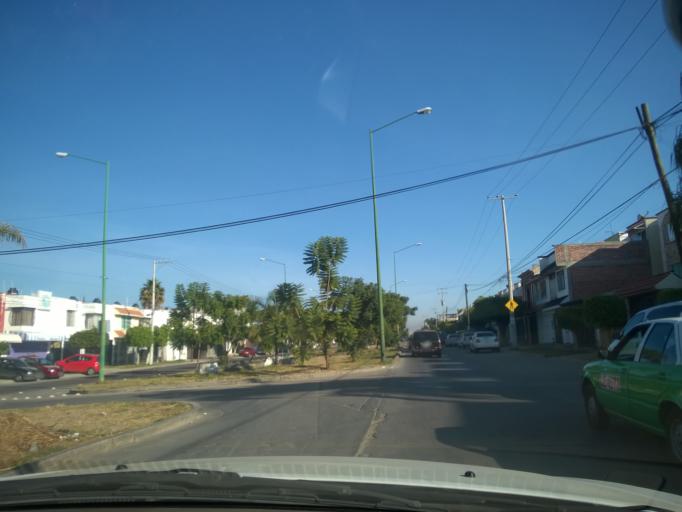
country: MX
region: Guanajuato
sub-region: Leon
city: San Jose de Duran (Los Troncoso)
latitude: 21.0861
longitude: -101.6431
